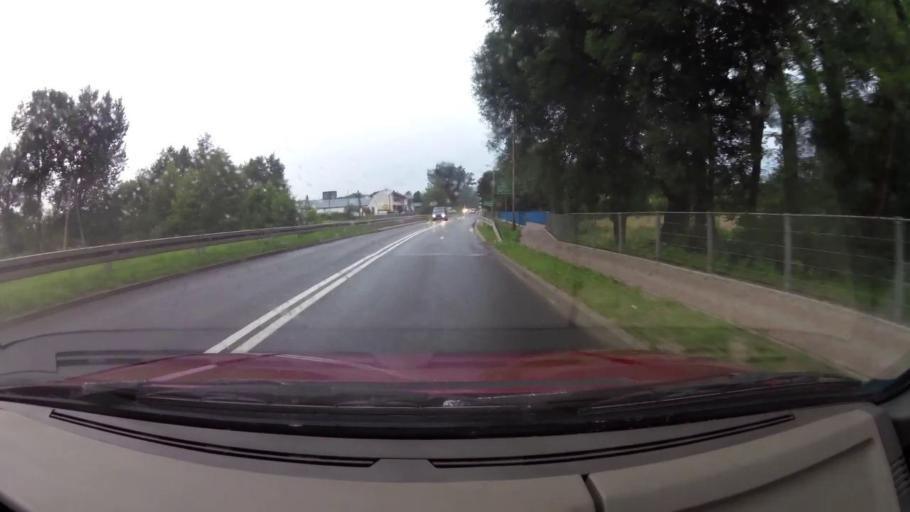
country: PL
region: West Pomeranian Voivodeship
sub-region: Powiat stargardzki
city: Stara Dabrowa
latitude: 53.3827
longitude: 15.1731
